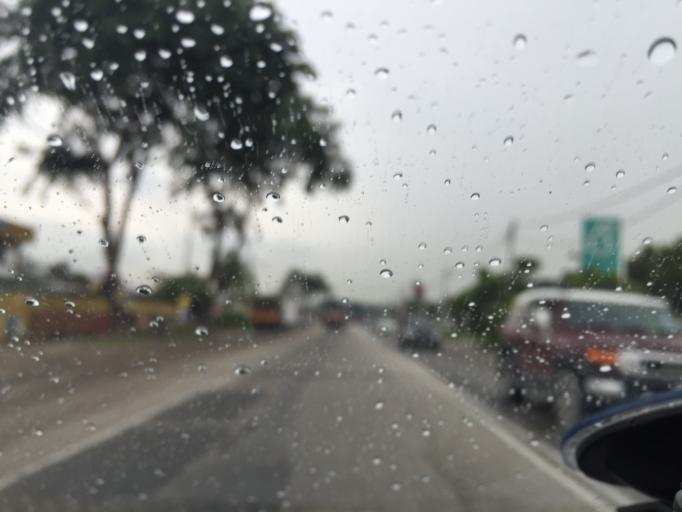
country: MY
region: Selangor
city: Subang Jaya
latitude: 3.0124
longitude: 101.5215
